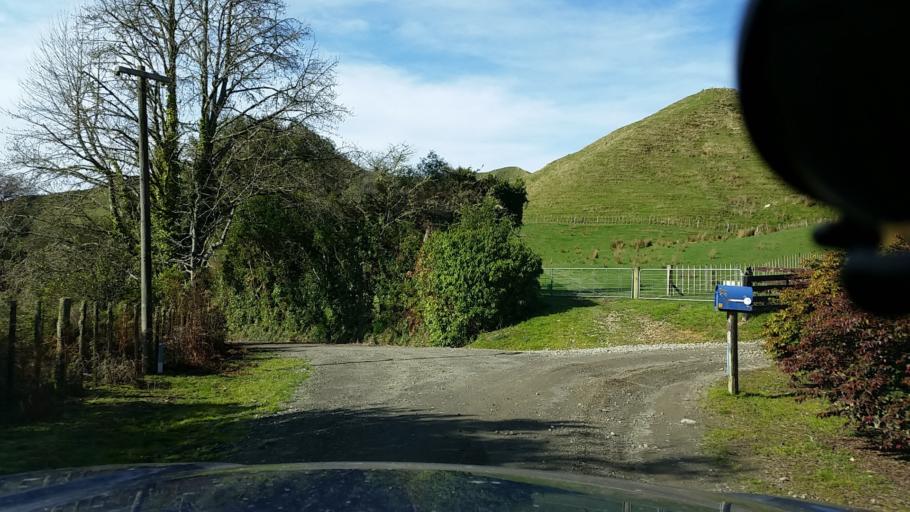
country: NZ
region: Taranaki
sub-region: New Plymouth District
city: Waitara
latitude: -39.0528
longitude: 174.7501
